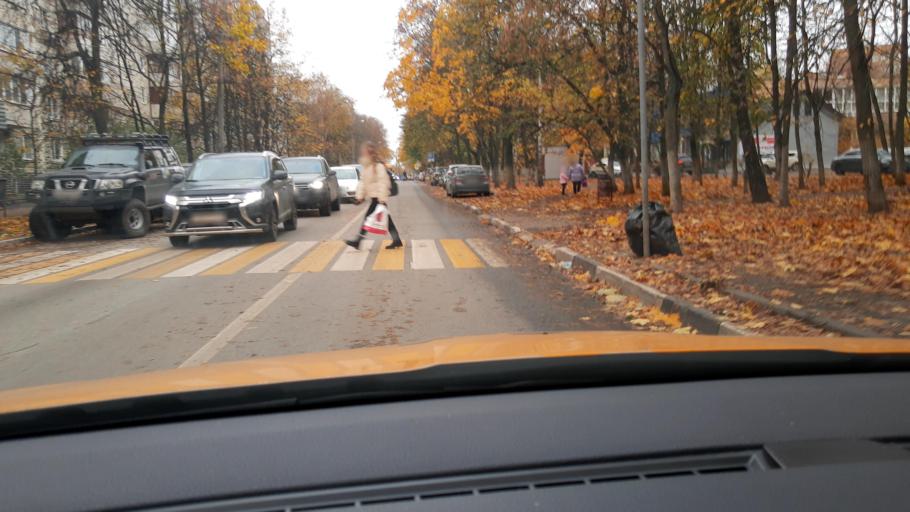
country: RU
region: Moskovskaya
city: Odintsovo
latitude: 55.6809
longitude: 37.2561
